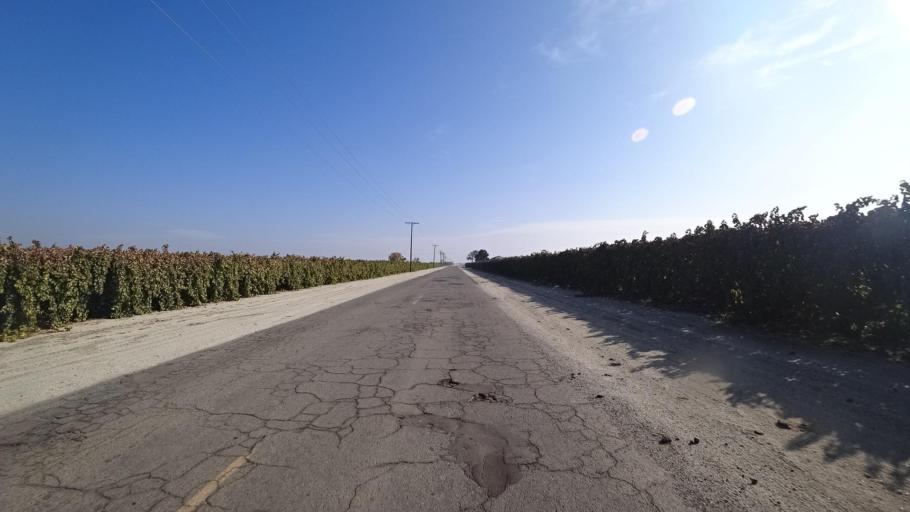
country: US
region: California
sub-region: Kern County
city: McFarland
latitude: 35.6814
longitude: -119.2082
